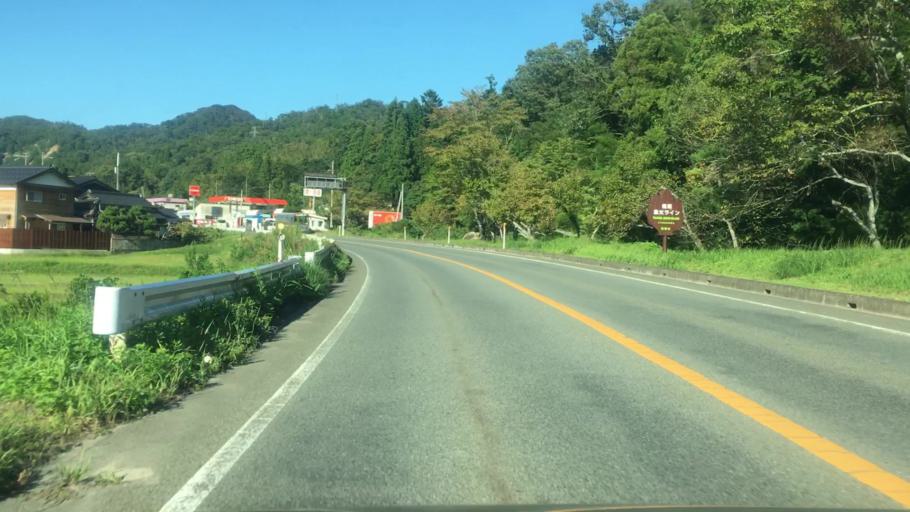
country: JP
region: Hyogo
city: Toyooka
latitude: 35.5587
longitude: 134.8505
